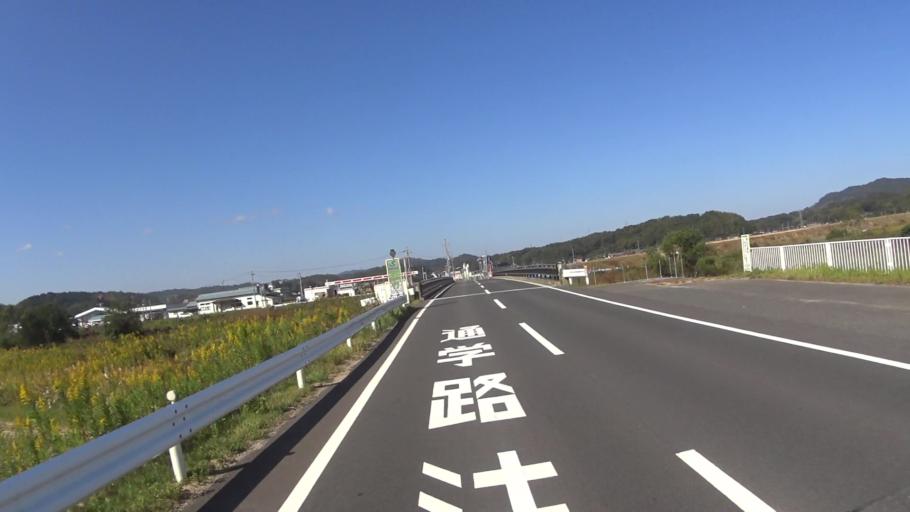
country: JP
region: Kyoto
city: Miyazu
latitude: 35.6698
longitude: 135.0888
